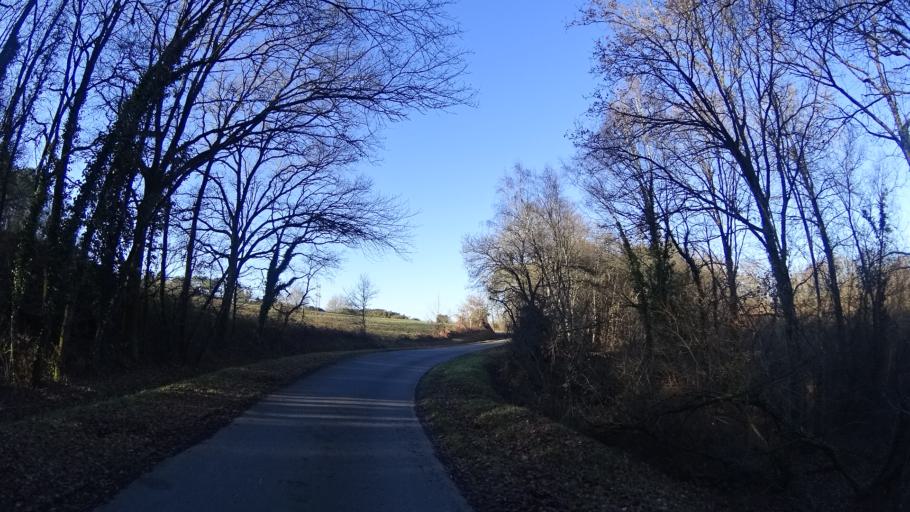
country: FR
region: Brittany
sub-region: Departement du Morbihan
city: Saint-Jacut-les-Pins
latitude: 47.6599
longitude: -2.2059
